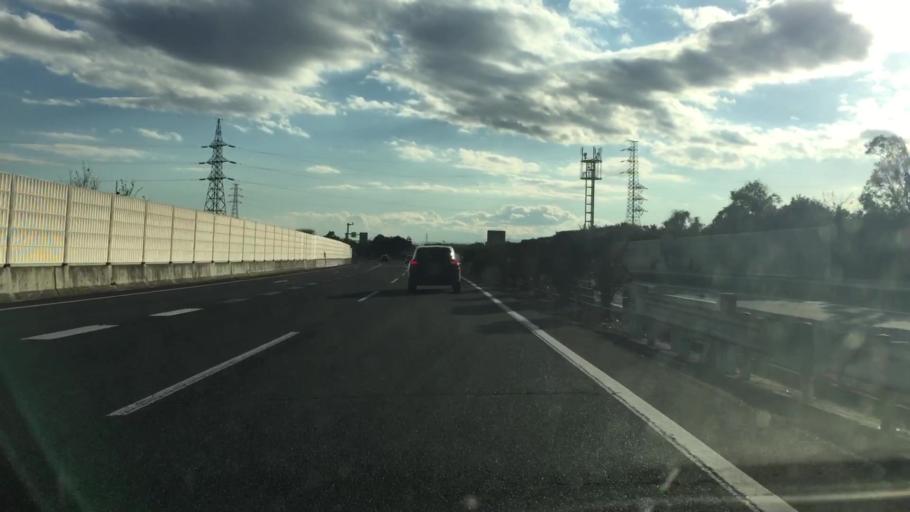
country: JP
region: Gunma
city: Shibukawa
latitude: 36.4708
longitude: 139.0128
